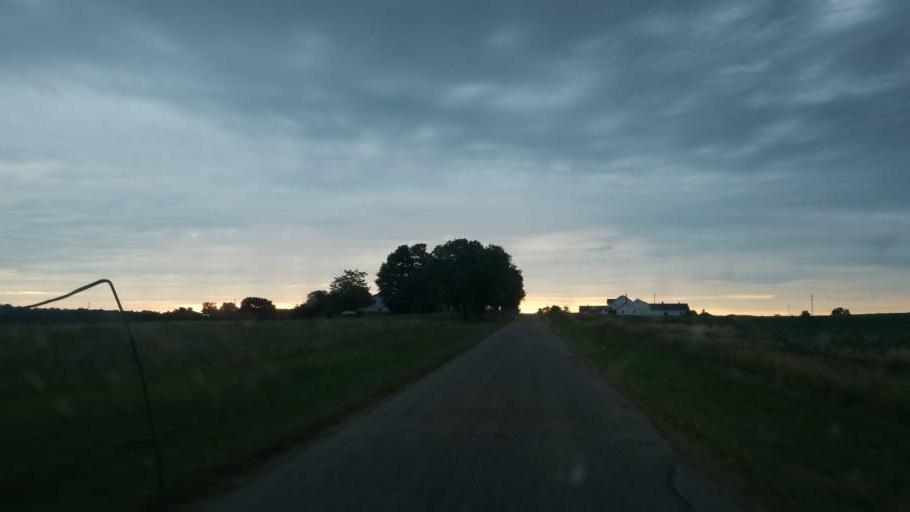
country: US
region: Ohio
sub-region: Defiance County
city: Hicksville
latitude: 41.3681
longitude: -84.7723
